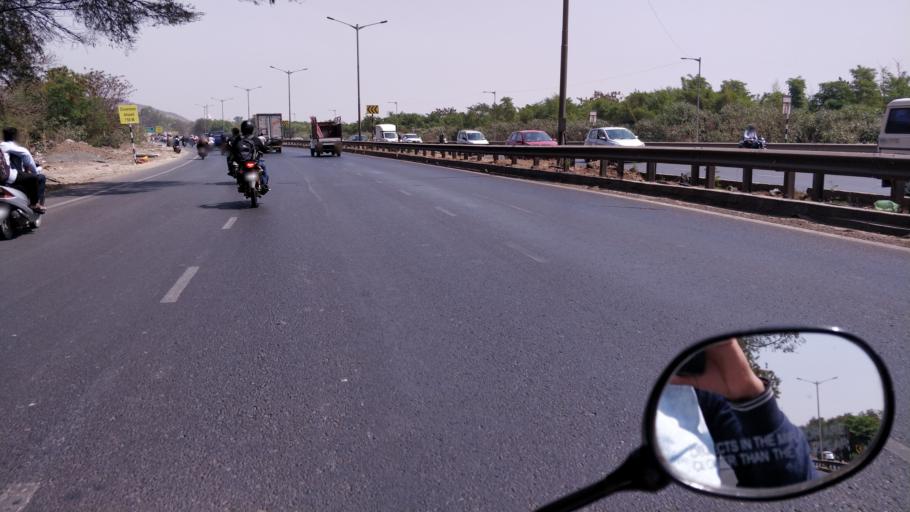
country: IN
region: Maharashtra
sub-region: Pune Division
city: Shivaji Nagar
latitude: 18.5289
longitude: 73.7782
